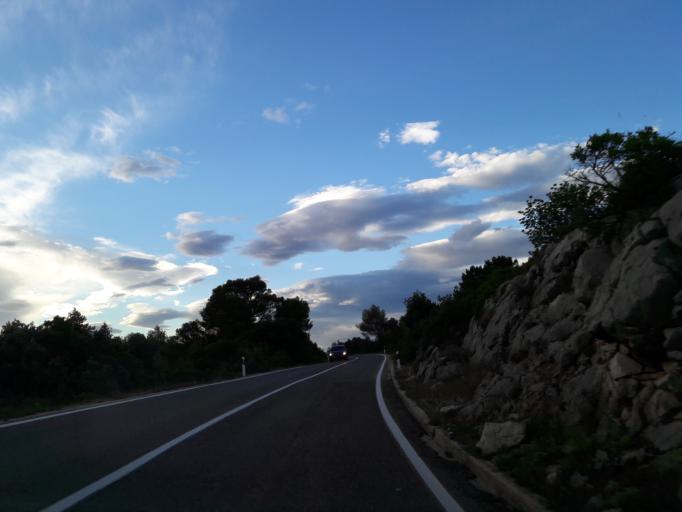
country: BA
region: Federation of Bosnia and Herzegovina
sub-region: Hercegovacko-Bosanski Kanton
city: Neum
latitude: 42.8904
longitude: 17.4988
